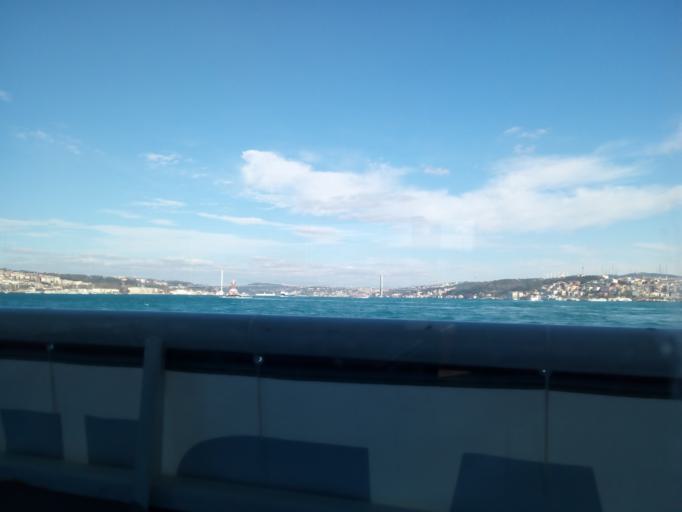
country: TR
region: Istanbul
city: Eminoenue
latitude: 41.0280
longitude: 28.9967
